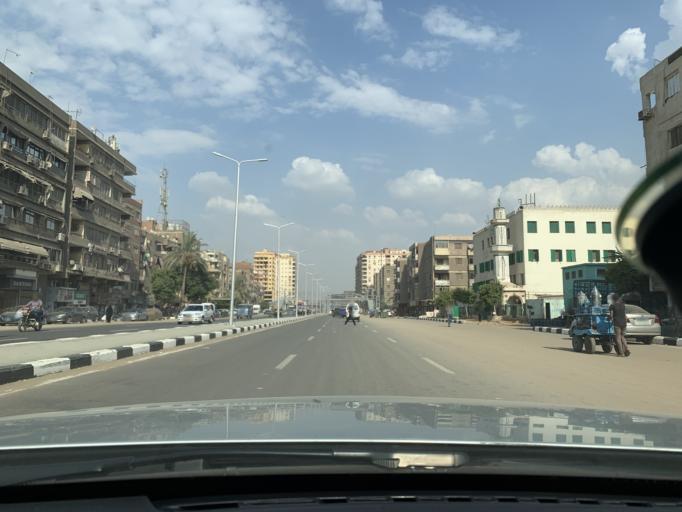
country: EG
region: Muhafazat al Qahirah
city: Cairo
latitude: 30.1325
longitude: 31.2820
